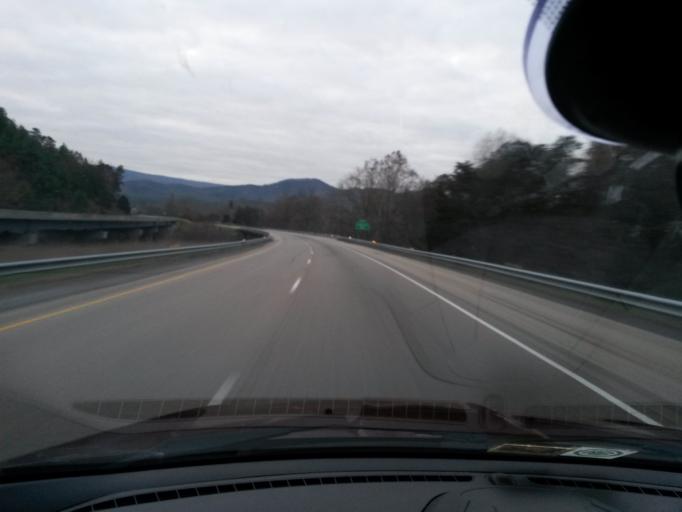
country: US
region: Virginia
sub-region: Alleghany County
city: Clifton Forge
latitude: 37.8089
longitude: -79.7405
